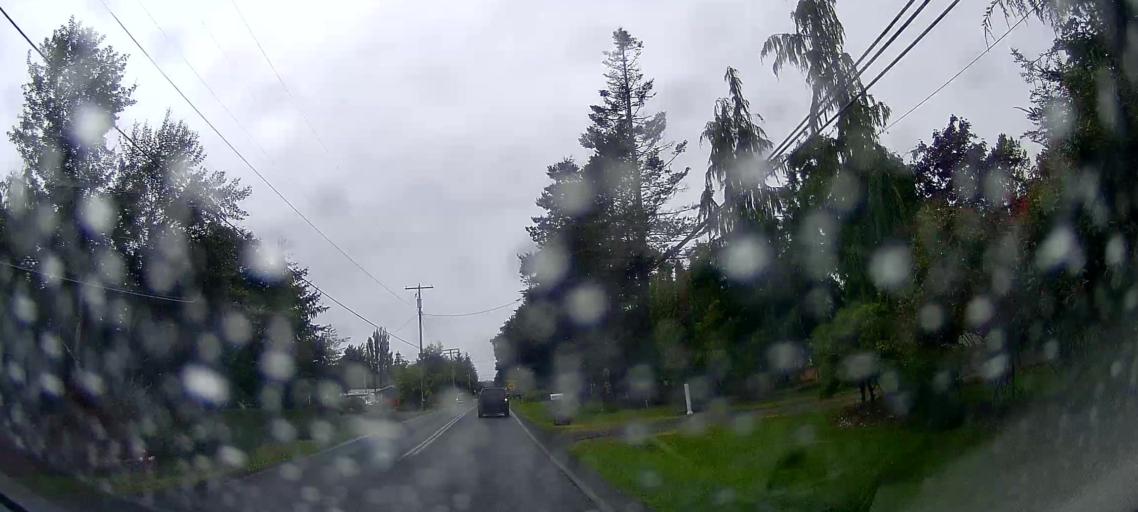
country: US
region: Washington
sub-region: Whatcom County
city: Marietta-Alderwood
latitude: 48.7833
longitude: -122.5535
